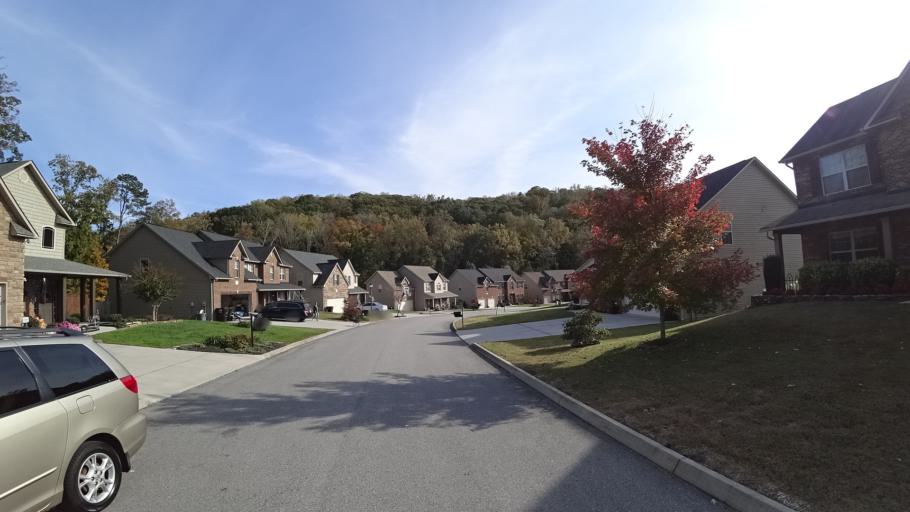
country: US
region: Tennessee
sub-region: Knox County
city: Farragut
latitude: 35.9132
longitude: -84.1817
